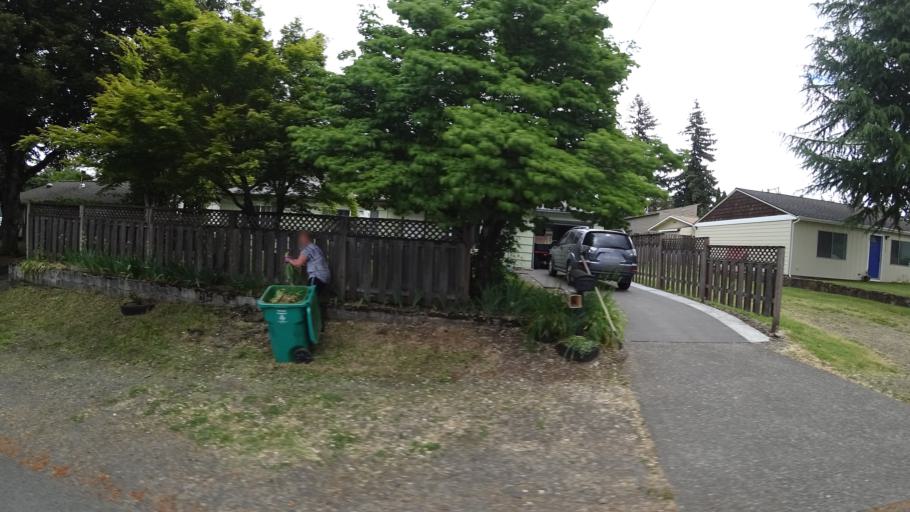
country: US
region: Oregon
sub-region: Clackamas County
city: Happy Valley
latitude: 45.5023
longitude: -122.5075
